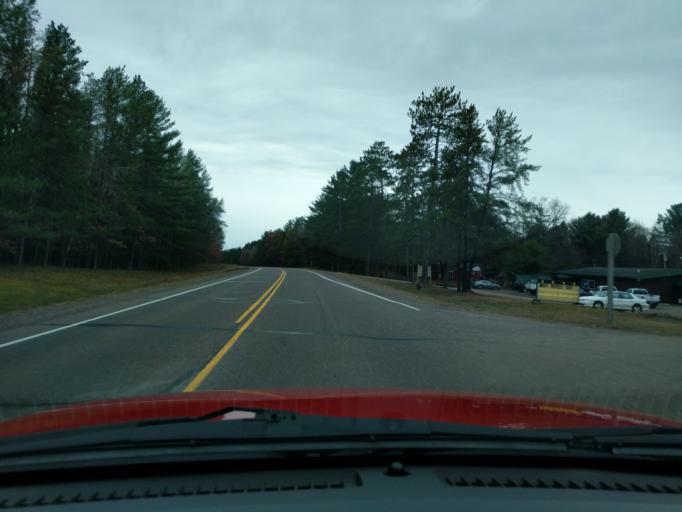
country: US
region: Wisconsin
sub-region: Washburn County
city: Spooner
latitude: 45.8240
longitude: -91.9388
